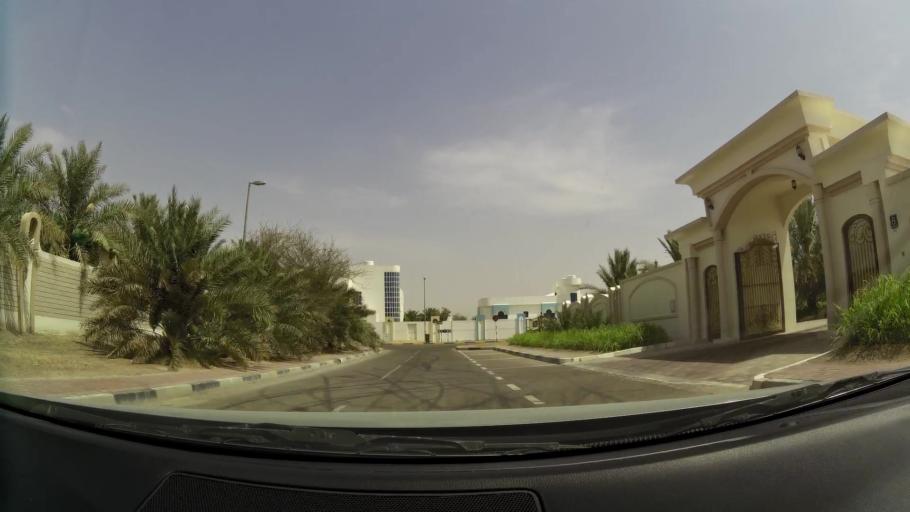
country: AE
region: Abu Dhabi
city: Al Ain
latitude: 24.1763
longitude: 55.7168
